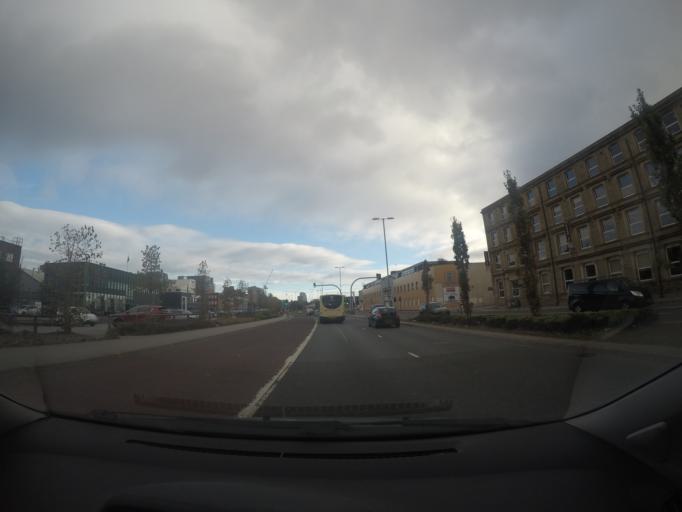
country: GB
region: England
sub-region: City and Borough of Leeds
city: Leeds
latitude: 53.8017
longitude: -1.5696
